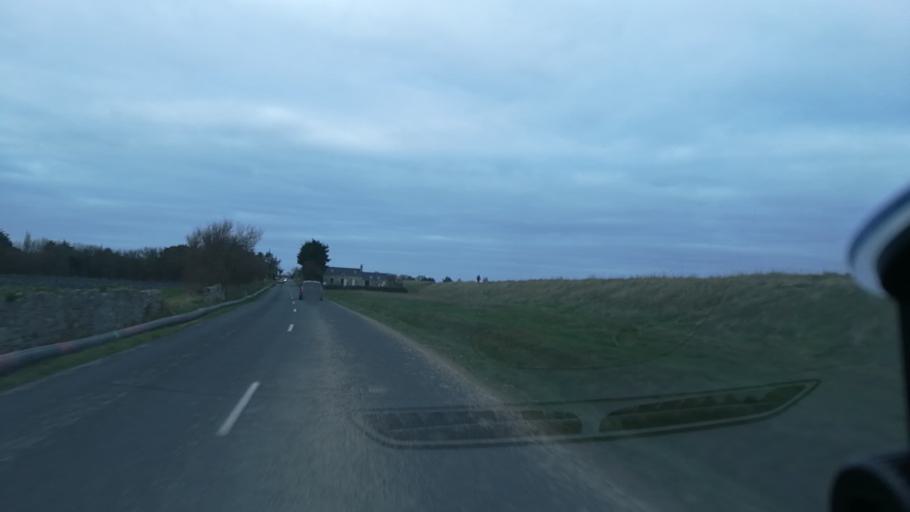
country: FR
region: Lower Normandy
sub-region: Departement de la Manche
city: Reville
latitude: 49.6045
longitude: -1.2591
